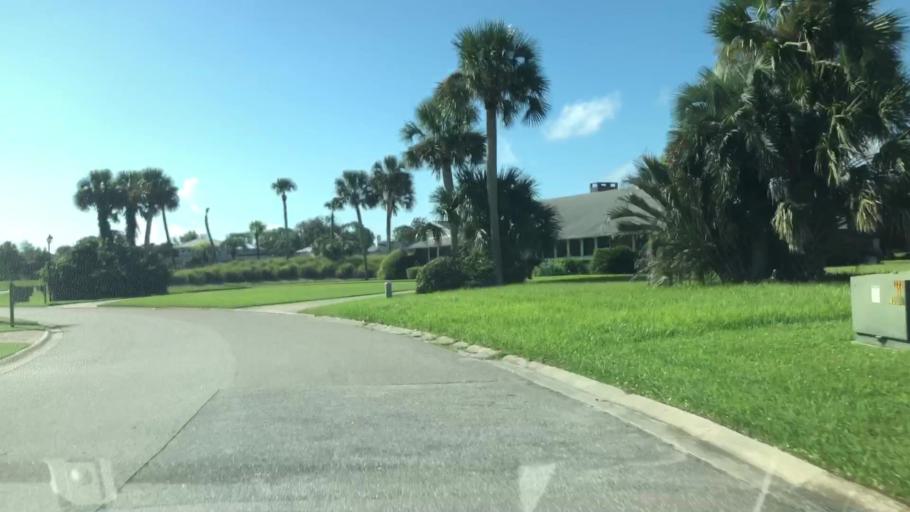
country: US
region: Florida
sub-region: Saint Johns County
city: Ponte Vedra Beach
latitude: 30.2337
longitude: -81.3837
